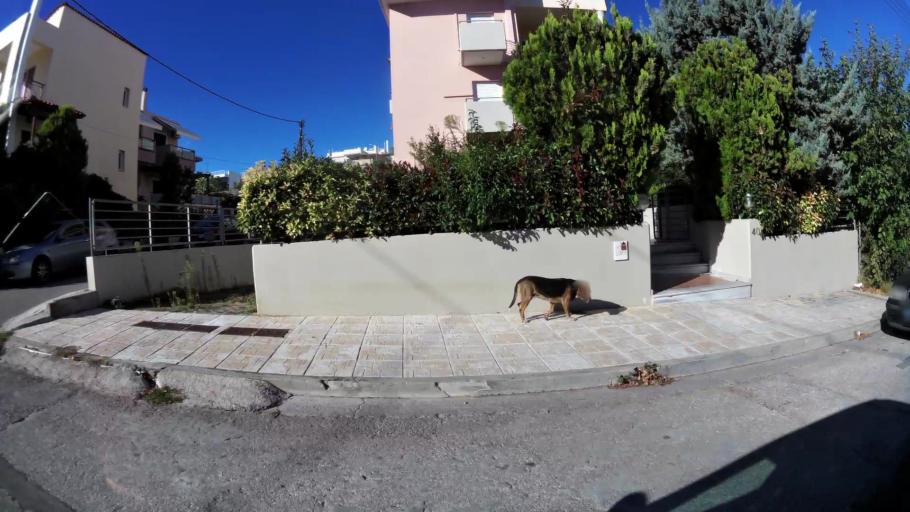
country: GR
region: Attica
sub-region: Nomarchia Anatolikis Attikis
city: Leondarion
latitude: 37.9777
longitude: 23.8486
